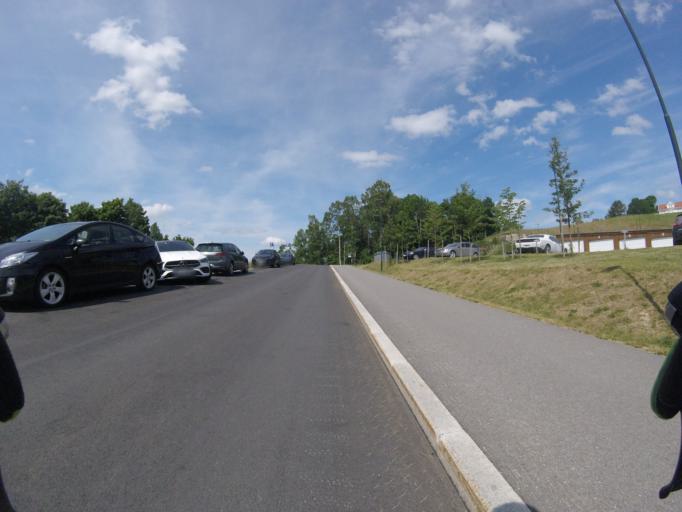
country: NO
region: Akershus
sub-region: Skedsmo
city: Lillestrom
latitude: 59.9774
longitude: 11.0238
